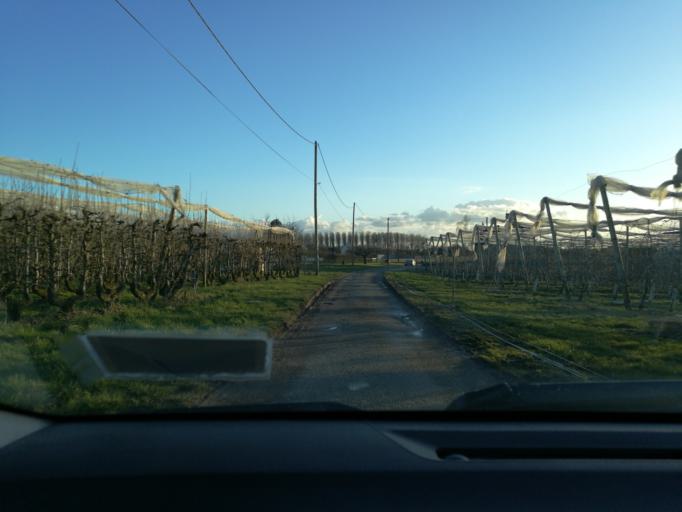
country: FR
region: Centre
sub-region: Departement du Loiret
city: Semoy
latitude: 47.9401
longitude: 1.9649
